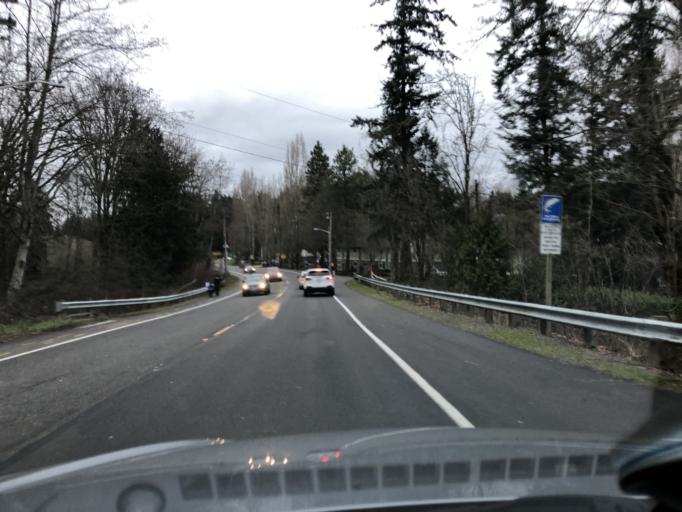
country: US
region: Washington
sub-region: King County
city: Des Moines
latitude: 47.3893
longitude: -122.3121
